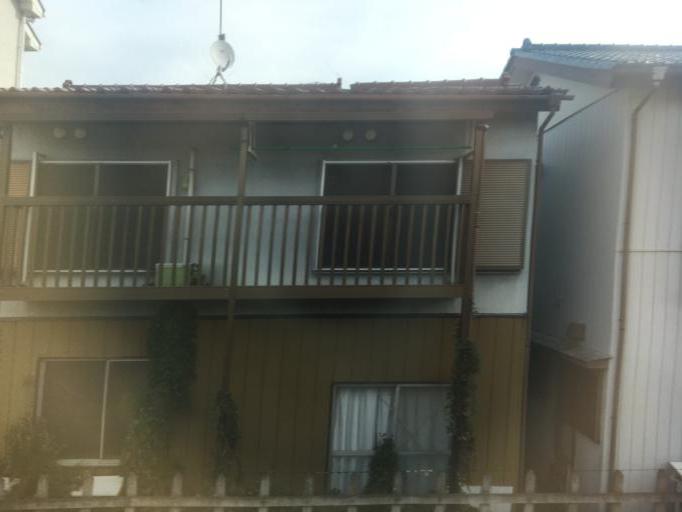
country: JP
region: Saitama
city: Sayama
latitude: 35.8162
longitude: 139.4138
